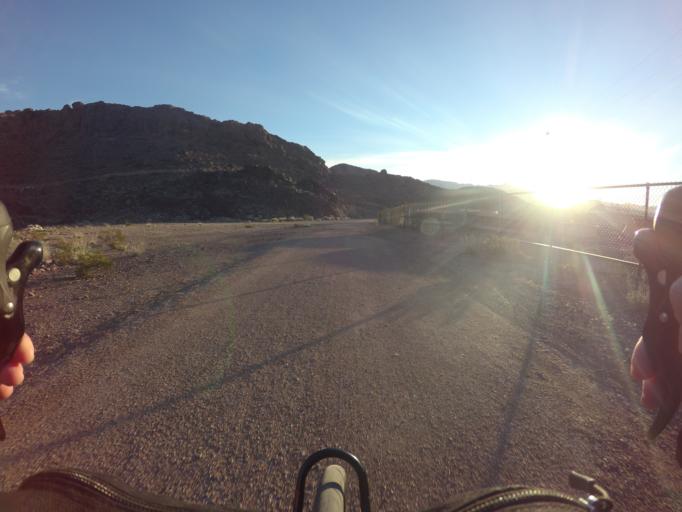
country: US
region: Nevada
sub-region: Clark County
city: Boulder City
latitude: 36.0200
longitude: -114.7478
